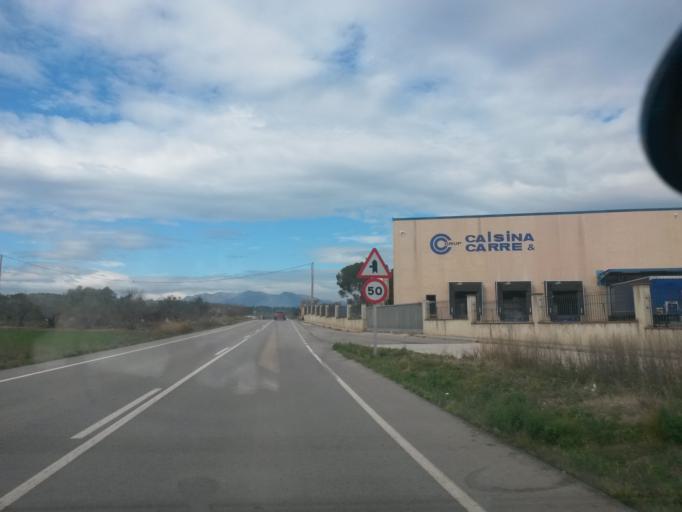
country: ES
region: Catalonia
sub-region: Provincia de Girona
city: Pont de Molins
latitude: 42.3163
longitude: 2.9364
